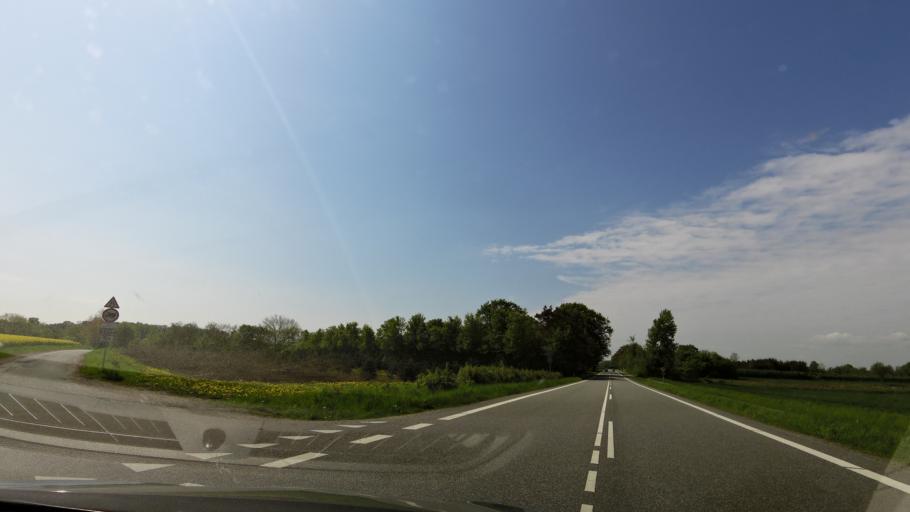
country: DK
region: South Denmark
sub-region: Nyborg Kommune
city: Ullerslev
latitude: 55.2759
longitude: 10.6825
